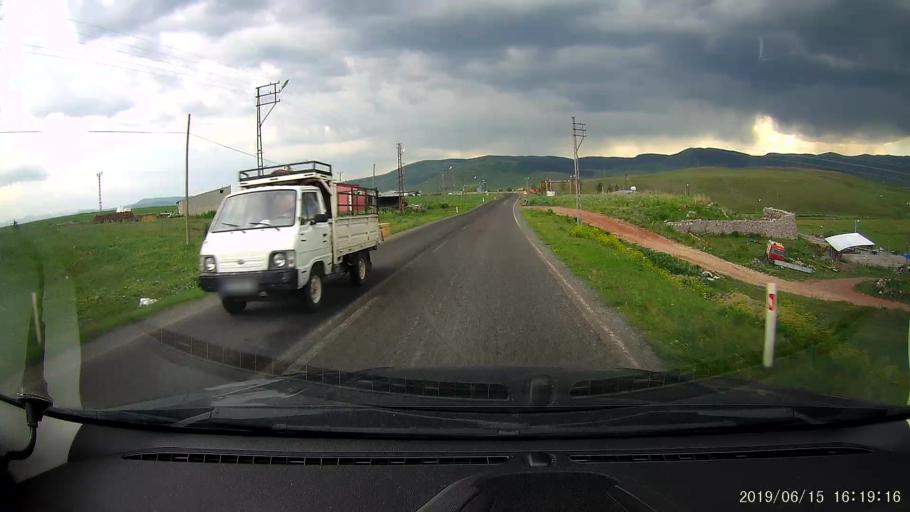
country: TR
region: Ardahan
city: Hanak
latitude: 41.2302
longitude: 42.8509
